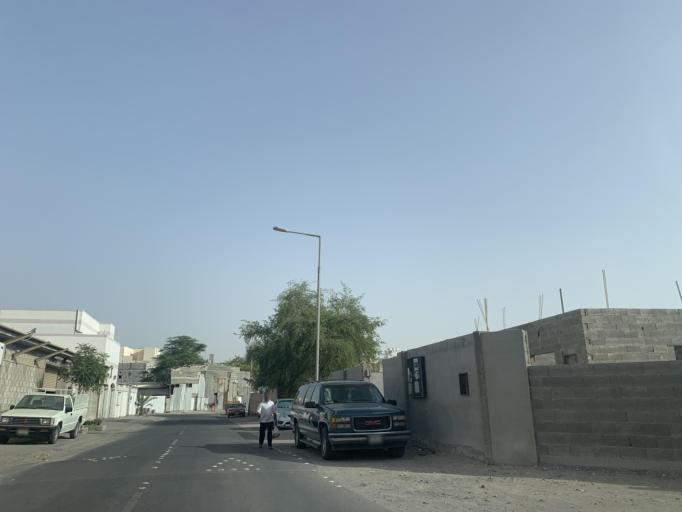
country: BH
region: Northern
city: Madinat `Isa
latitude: 26.1591
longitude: 50.5127
